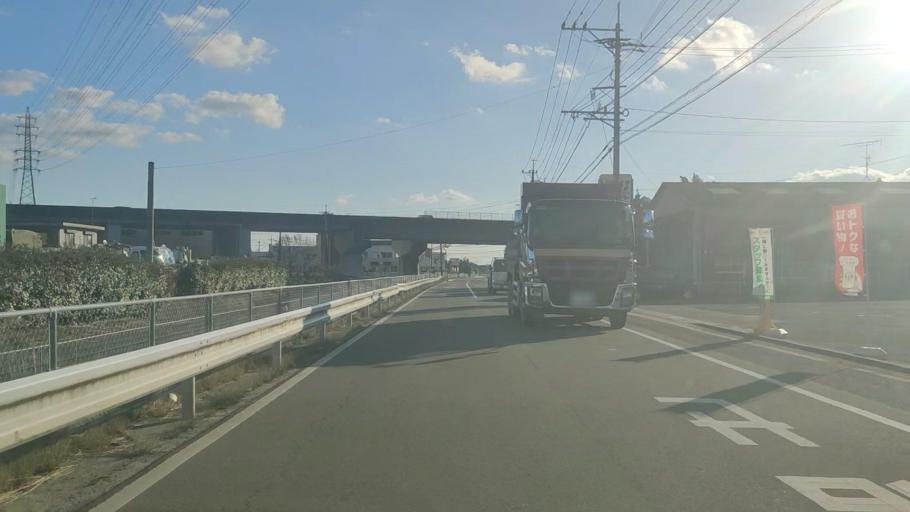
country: JP
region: Saga Prefecture
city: Saga-shi
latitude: 33.3193
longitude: 130.2672
